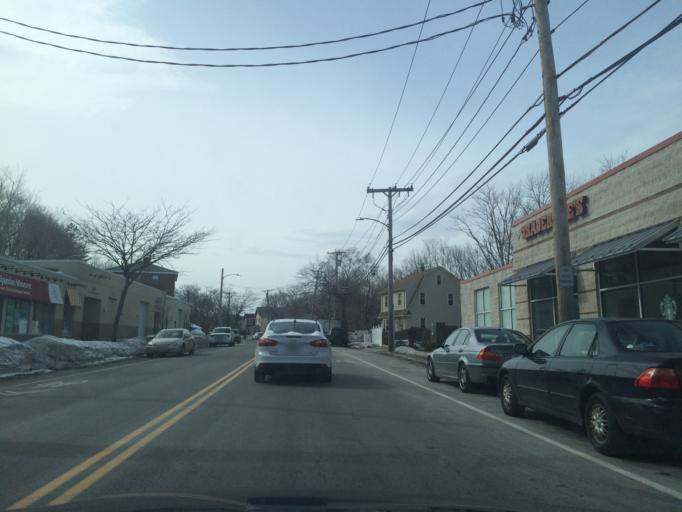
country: US
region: Massachusetts
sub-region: Middlesex County
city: Belmont
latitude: 42.4252
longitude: -71.1885
